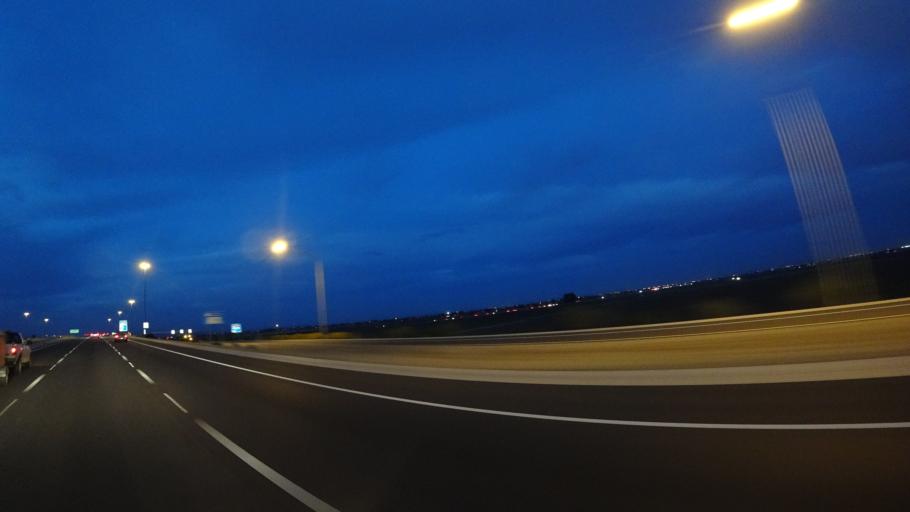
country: US
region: Arizona
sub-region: Maricopa County
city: Citrus Park
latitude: 33.6064
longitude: -112.4179
